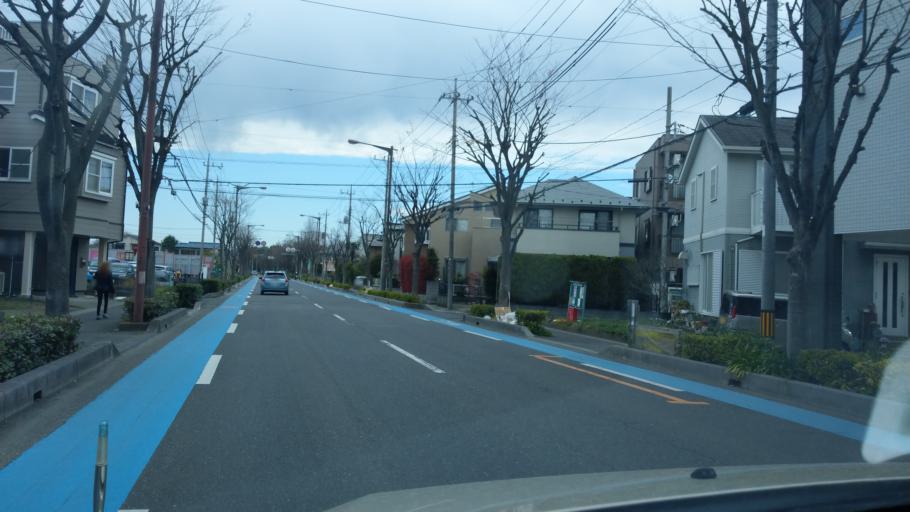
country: JP
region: Saitama
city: Yono
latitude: 35.8754
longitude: 139.6329
